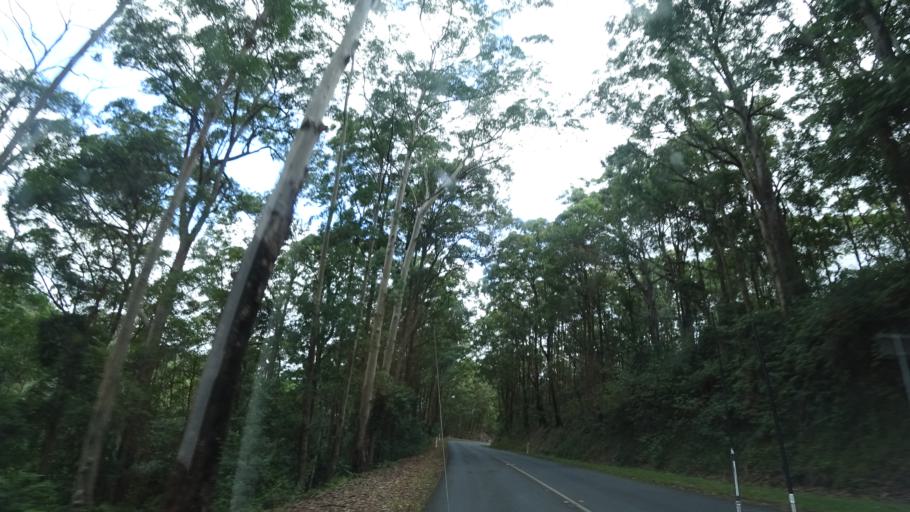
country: AU
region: Queensland
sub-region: Moreton Bay
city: Highvale
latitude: -27.3470
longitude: 152.7728
